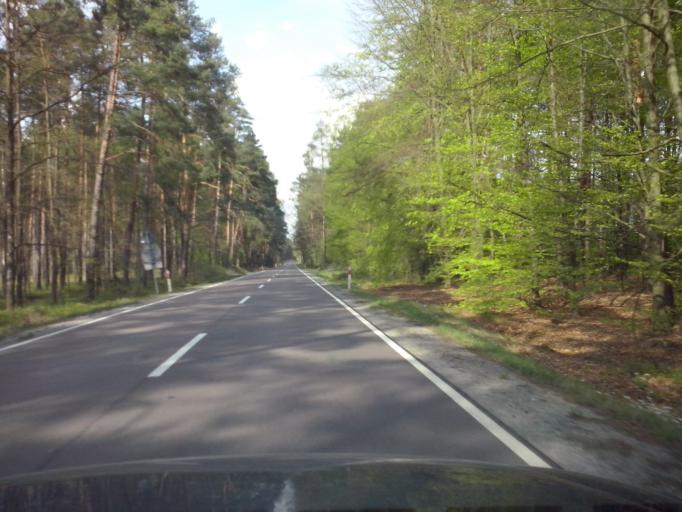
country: PL
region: Subcarpathian Voivodeship
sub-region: Powiat nizanski
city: Rudnik nad Sanem
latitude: 50.3817
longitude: 22.2595
